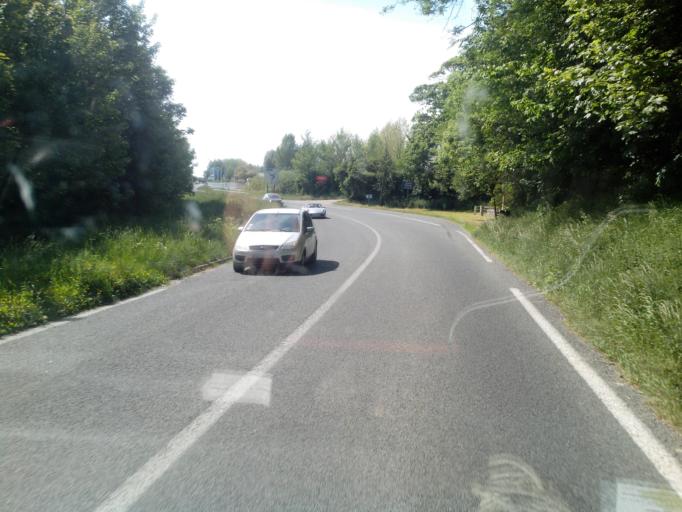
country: FR
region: Nord-Pas-de-Calais
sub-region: Departement du Pas-de-Calais
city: Saint-Josse
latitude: 50.5063
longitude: 1.6697
